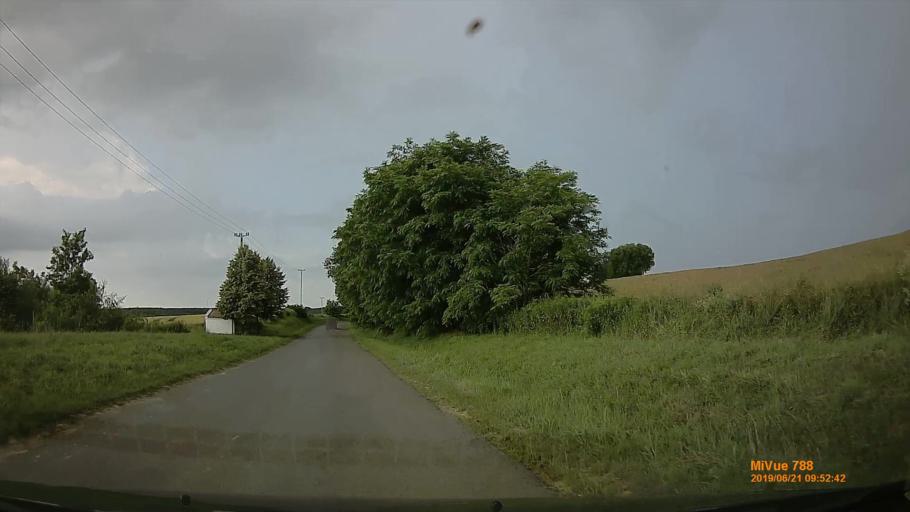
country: HU
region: Baranya
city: Sasd
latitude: 46.2416
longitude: 18.0142
